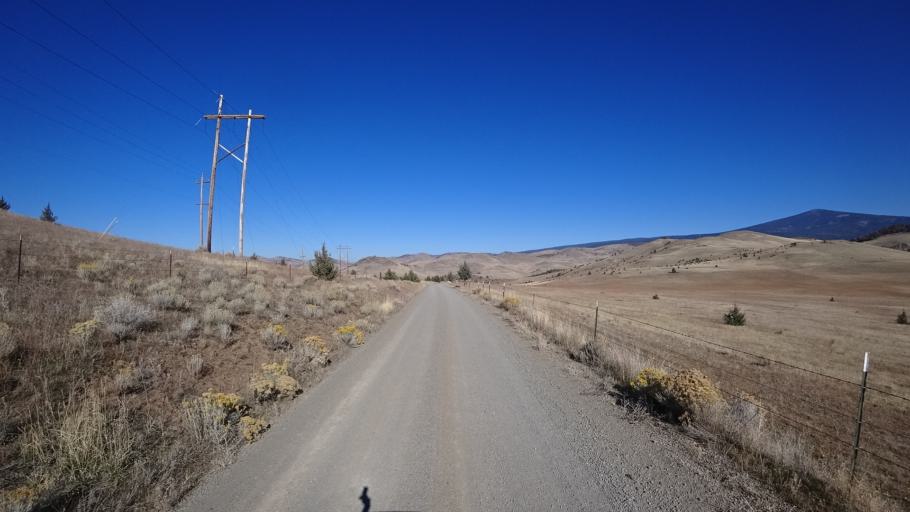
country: US
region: California
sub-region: Siskiyou County
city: Montague
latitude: 41.7739
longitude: -122.3588
